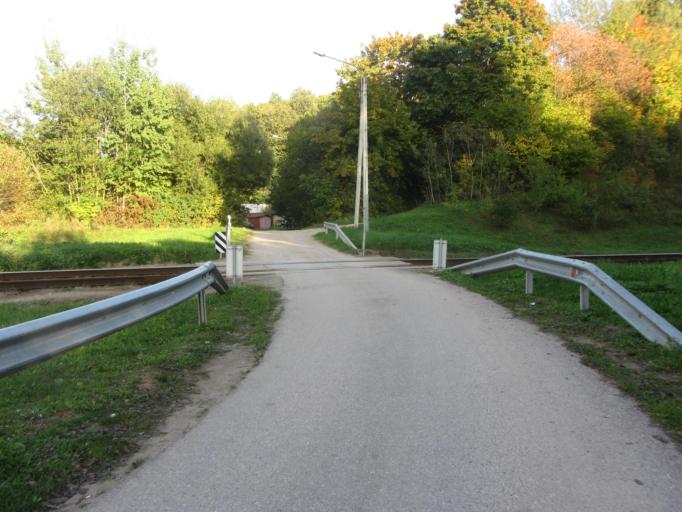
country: LT
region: Vilnius County
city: Lazdynai
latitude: 54.6389
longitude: 25.2131
